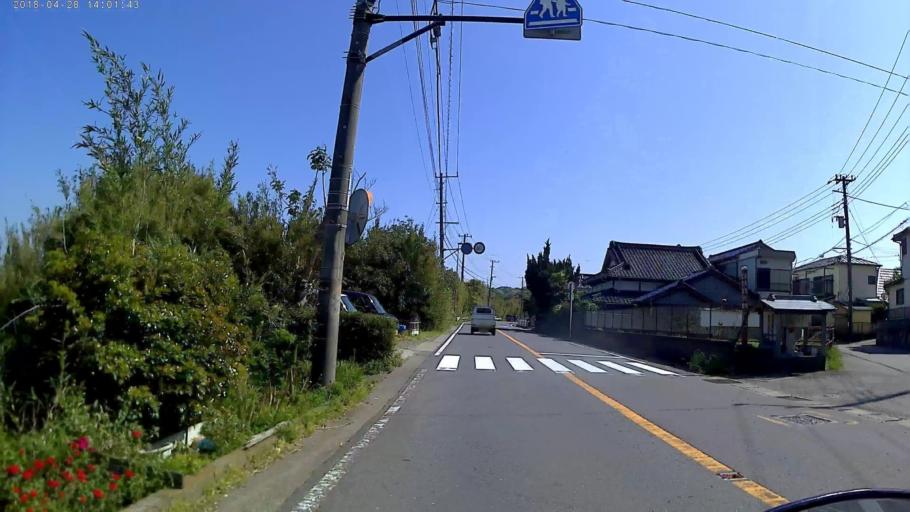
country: JP
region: Kanagawa
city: Miura
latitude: 35.1664
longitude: 139.6595
